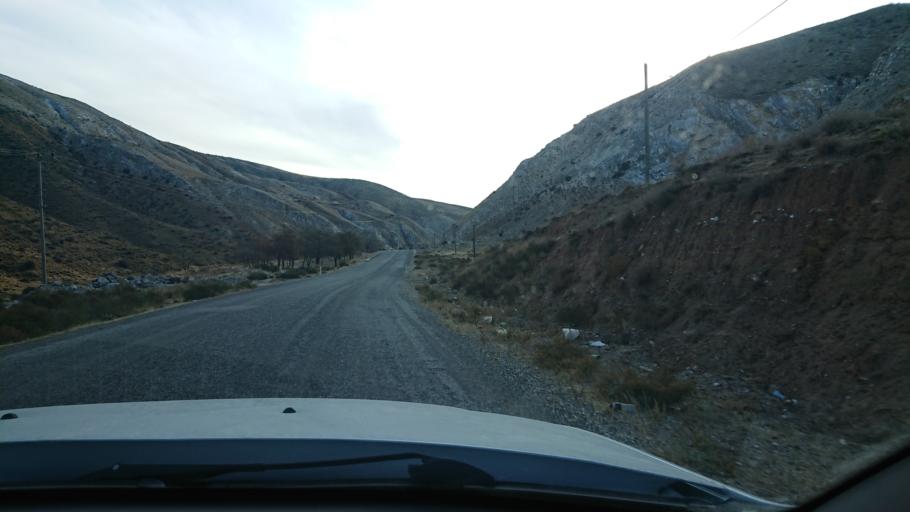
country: TR
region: Ankara
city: Sereflikochisar
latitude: 38.7551
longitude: 33.6932
